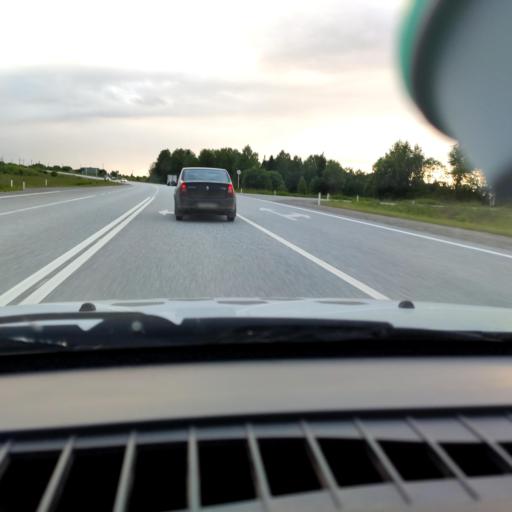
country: RU
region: Perm
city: Verkhnechusovskiye Gorodki
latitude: 58.2660
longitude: 57.3180
